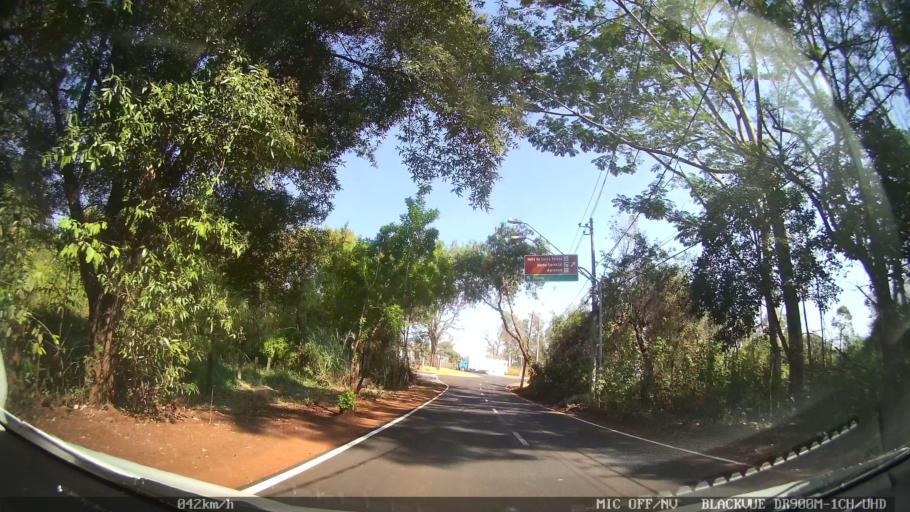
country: BR
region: Sao Paulo
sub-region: Ribeirao Preto
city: Ribeirao Preto
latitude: -21.2051
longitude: -47.8280
